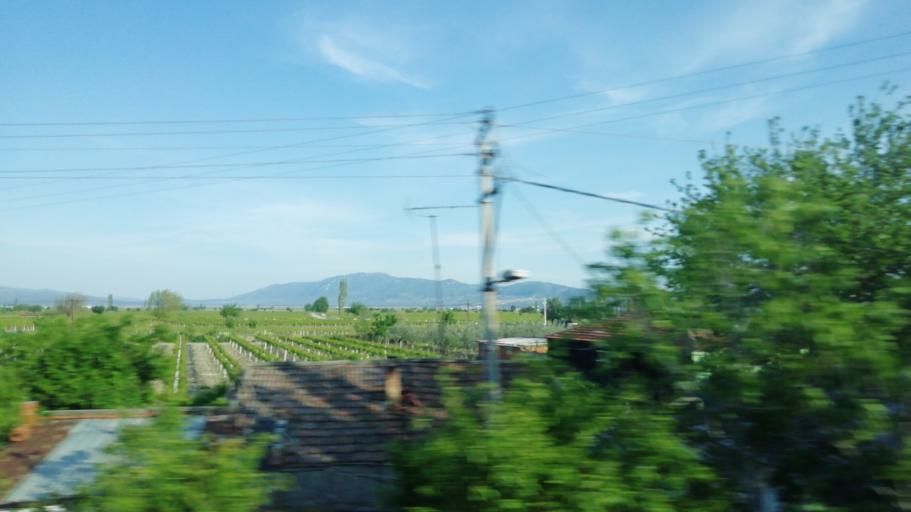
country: TR
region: Manisa
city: Saruhanli
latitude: 38.7559
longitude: 27.6334
